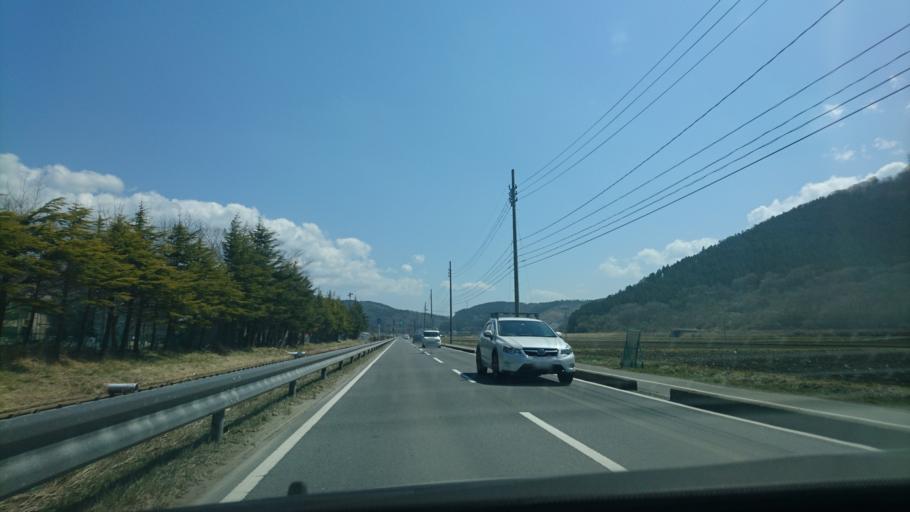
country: JP
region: Miyagi
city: Ishinomaki
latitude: 38.4472
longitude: 141.3564
